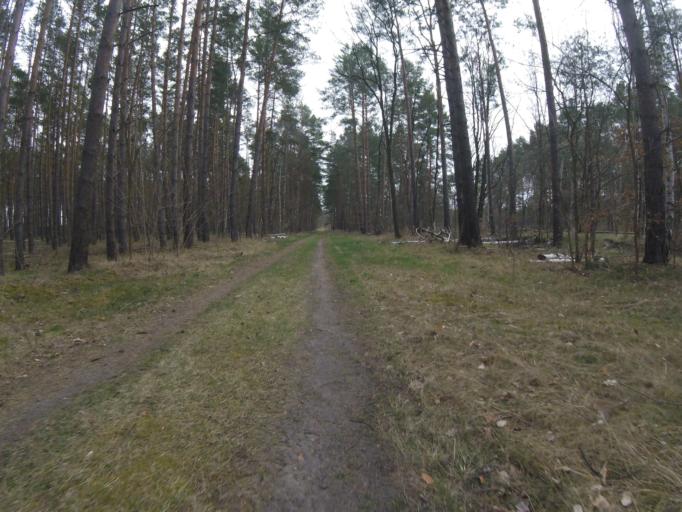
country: DE
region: Brandenburg
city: Schwerin
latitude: 52.1848
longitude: 13.6334
